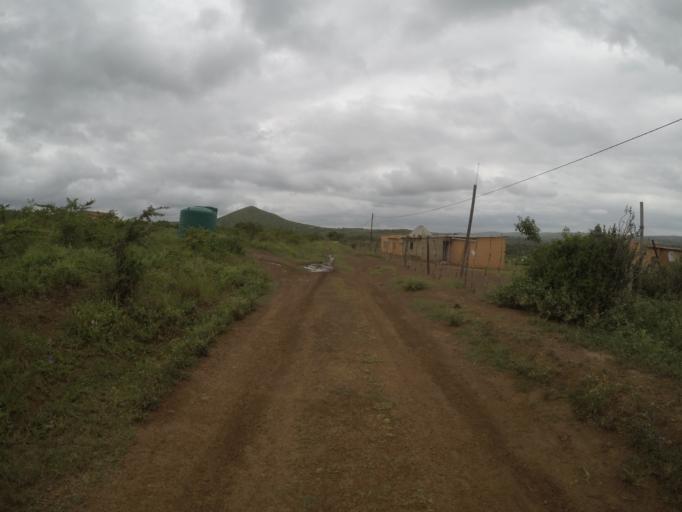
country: ZA
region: KwaZulu-Natal
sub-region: uThungulu District Municipality
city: Empangeni
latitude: -28.5873
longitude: 31.8624
